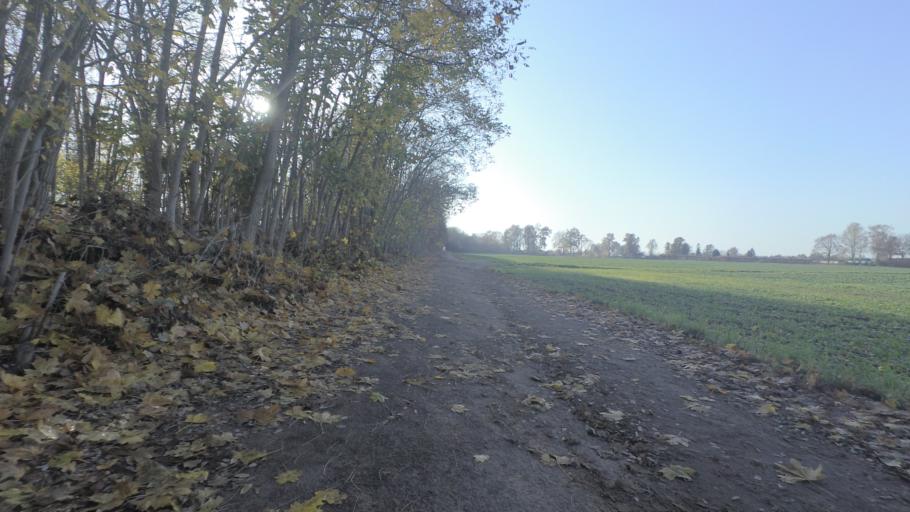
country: DE
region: Brandenburg
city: Zossen
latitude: 52.2095
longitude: 13.4297
